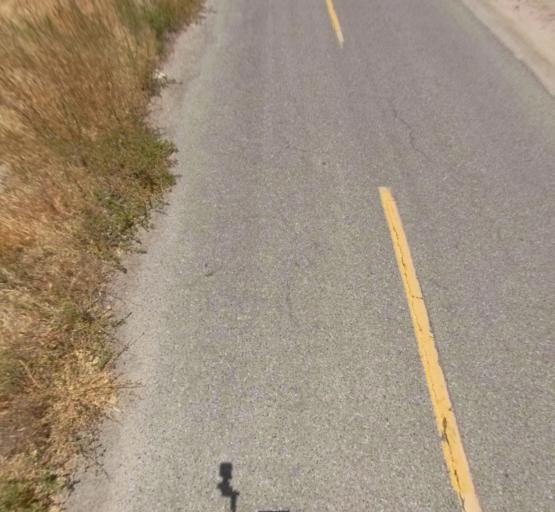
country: US
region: California
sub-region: Madera County
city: Parkwood
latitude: 36.9112
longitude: -120.1014
